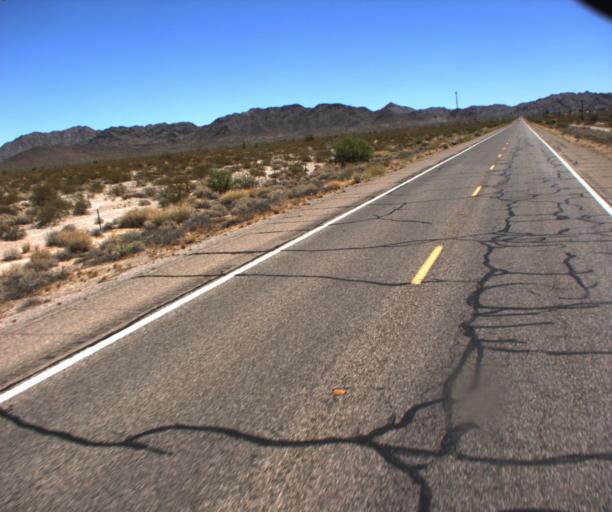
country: US
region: Arizona
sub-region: La Paz County
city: Salome
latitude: 33.7221
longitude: -113.7195
